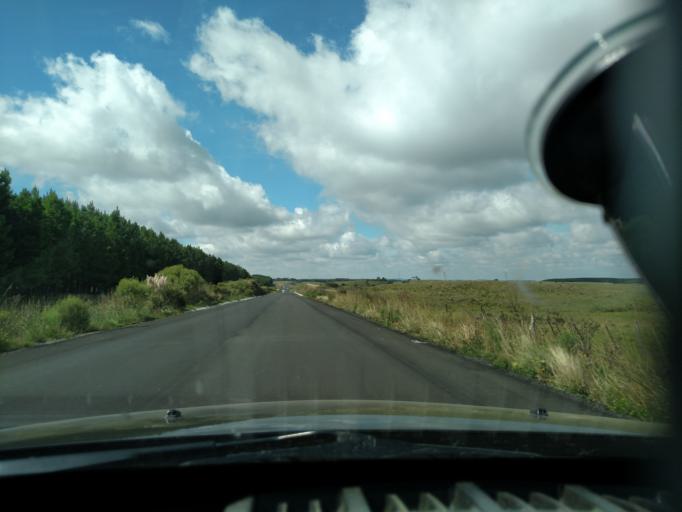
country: BR
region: Santa Catarina
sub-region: Lages
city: Lages
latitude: -28.0019
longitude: -50.0871
